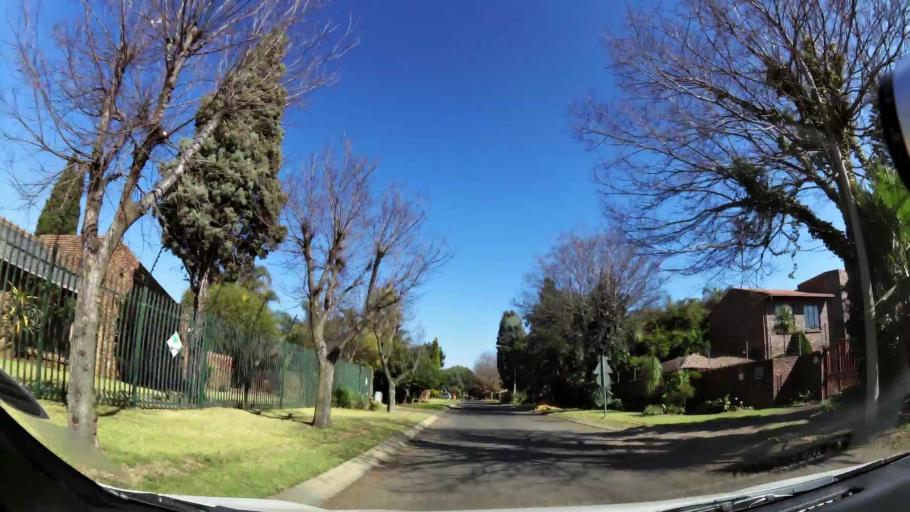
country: ZA
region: Gauteng
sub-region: Ekurhuleni Metropolitan Municipality
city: Germiston
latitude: -26.2998
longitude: 28.1016
